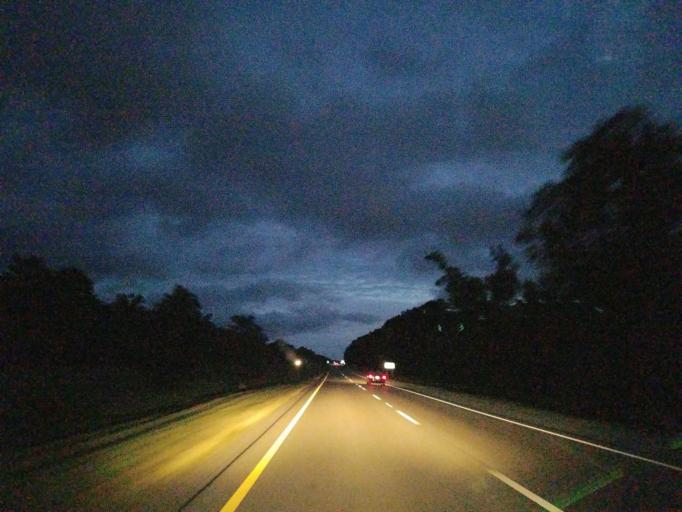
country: US
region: Mississippi
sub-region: Jones County
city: Sharon
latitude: 31.7993
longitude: -89.0543
